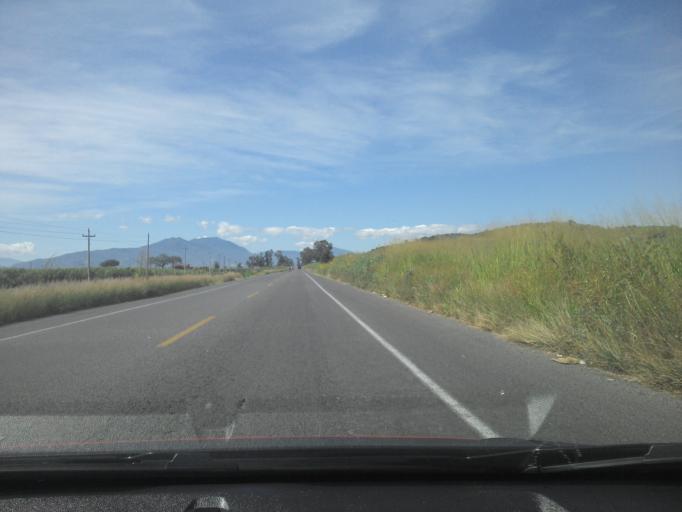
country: MX
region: Jalisco
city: El Refugio
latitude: 20.6658
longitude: -103.7647
